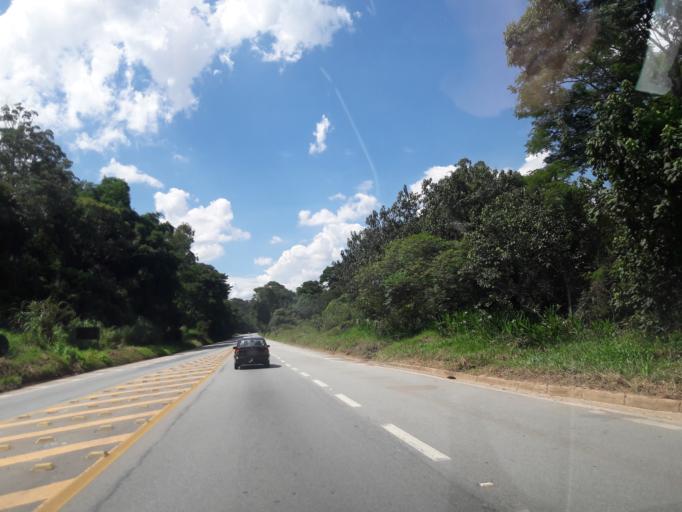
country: BR
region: Sao Paulo
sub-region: Francisco Morato
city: Francisco Morato
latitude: -23.3019
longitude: -46.8102
